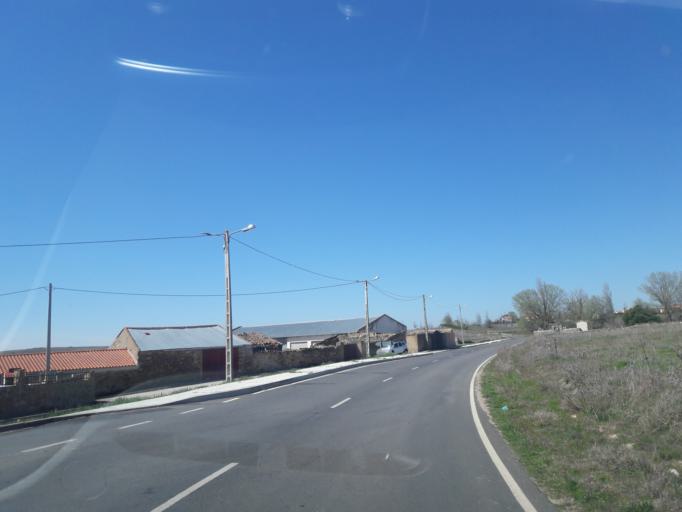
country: ES
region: Castille and Leon
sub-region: Provincia de Salamanca
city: Martinamor
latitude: 40.8071
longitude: -5.6003
